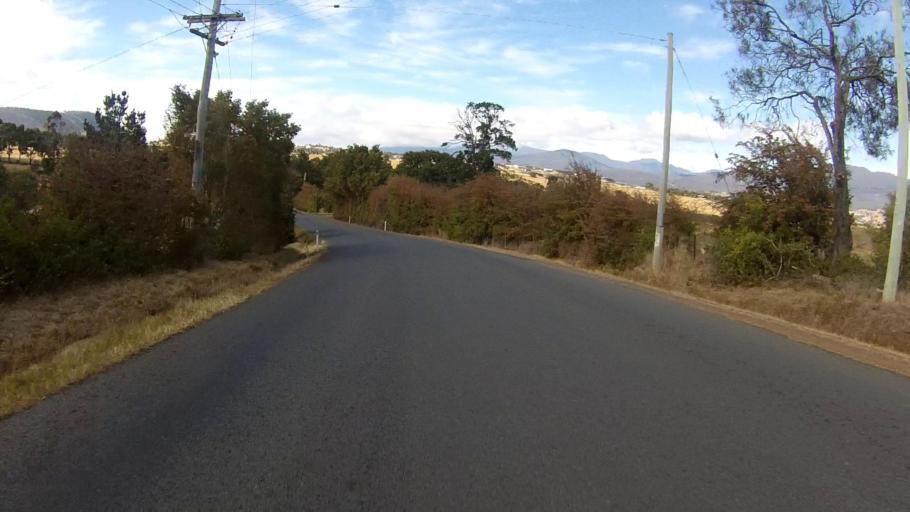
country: AU
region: Tasmania
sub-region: Brighton
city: Old Beach
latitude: -42.7525
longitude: 147.2790
